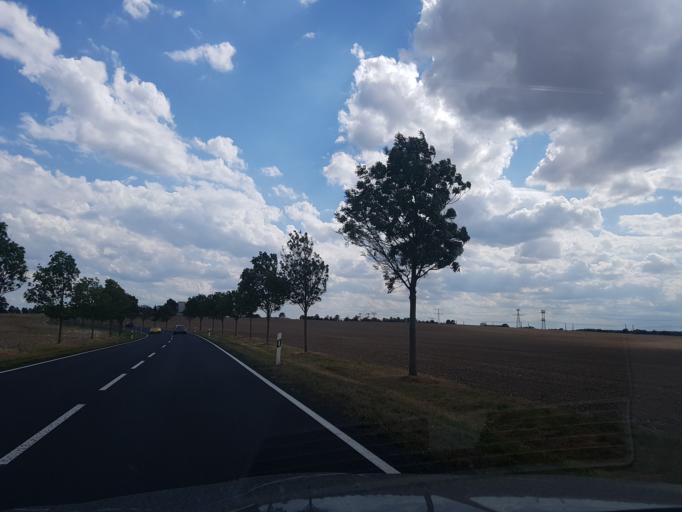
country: DE
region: Saxony
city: Priestewitz
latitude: 51.2448
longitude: 13.5477
